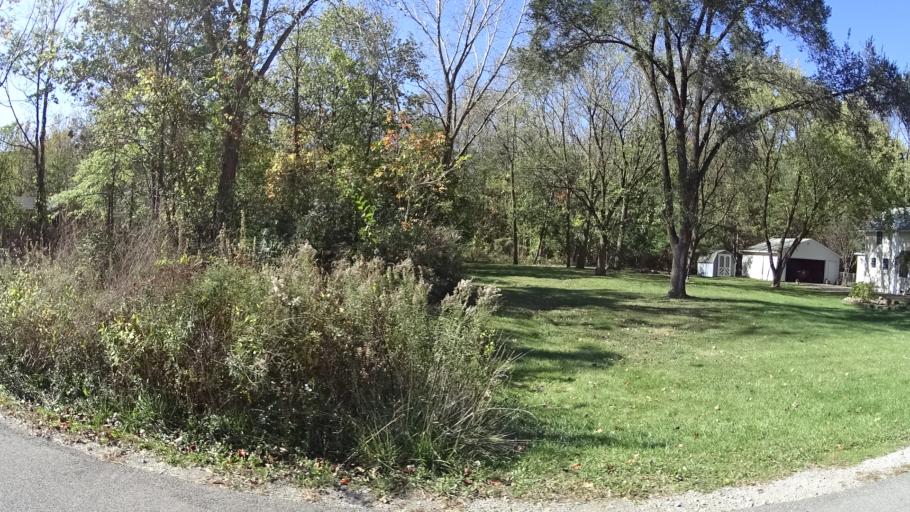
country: US
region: Ohio
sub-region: Lorain County
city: Lorain
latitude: 41.4351
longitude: -82.1699
